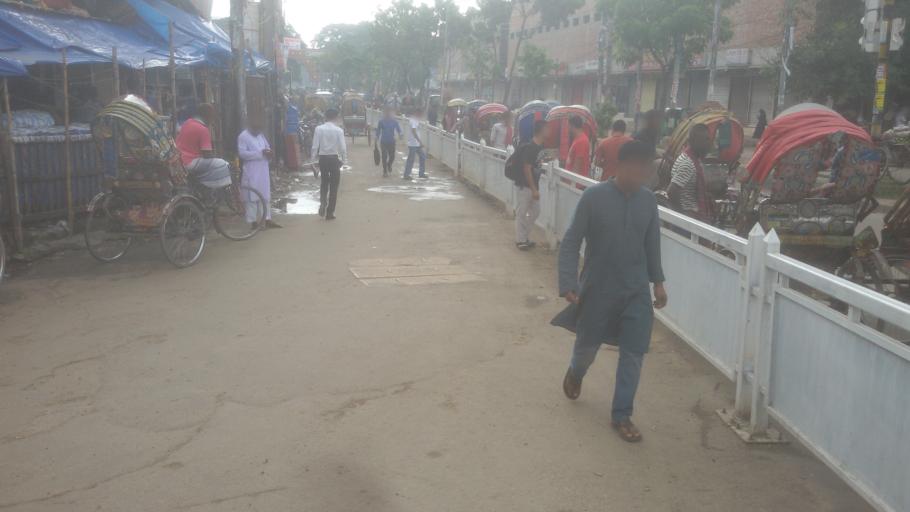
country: BD
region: Dhaka
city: Azimpur
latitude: 23.7324
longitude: 90.3852
